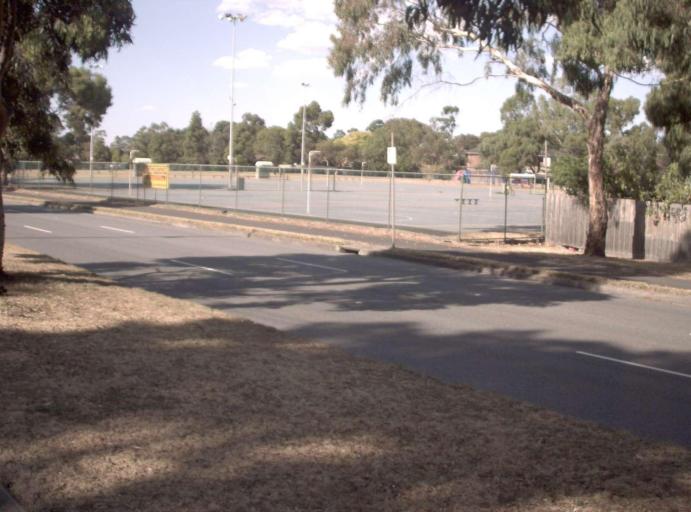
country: AU
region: Victoria
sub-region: Monash
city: Oakleigh South
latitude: -37.9350
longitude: 145.0803
